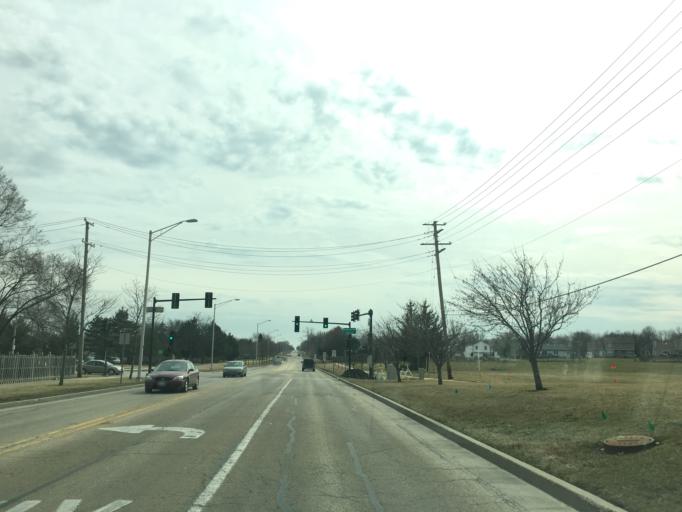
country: US
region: Illinois
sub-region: Cook County
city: Schaumburg
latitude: 42.0375
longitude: -88.1191
